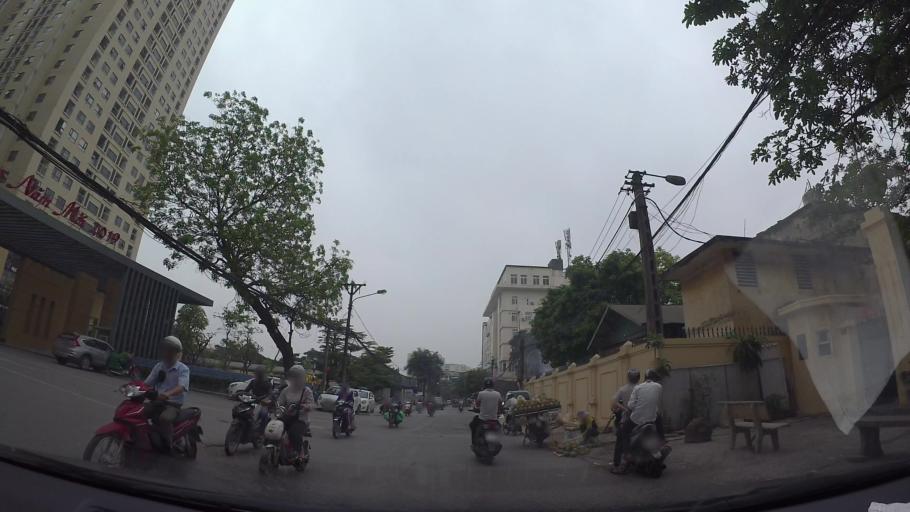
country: VN
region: Ha Noi
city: Hai BaTrung
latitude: 20.9889
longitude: 105.8659
